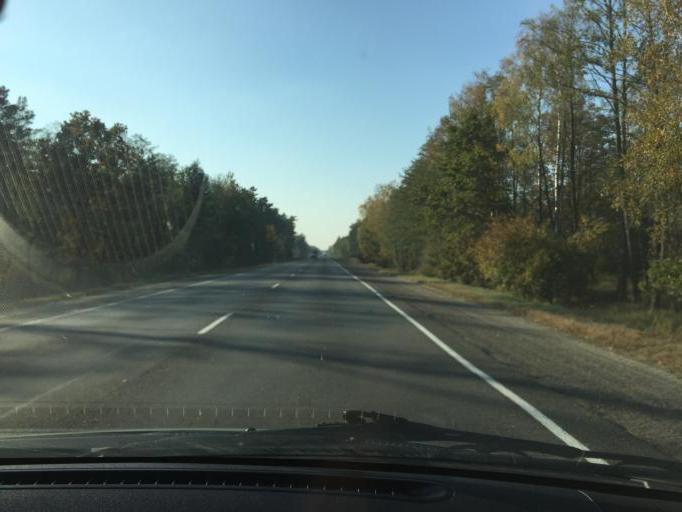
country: BY
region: Brest
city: Mikashevichy
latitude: 52.2427
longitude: 27.4603
